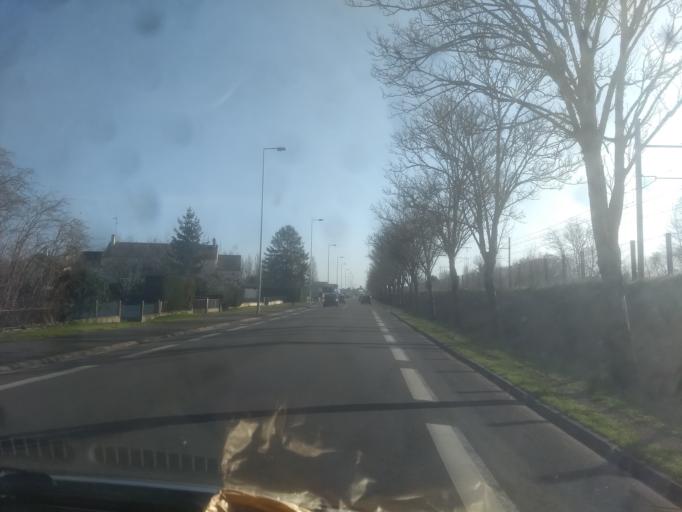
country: FR
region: Centre
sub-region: Departement du Cher
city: Bourges
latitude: 47.0945
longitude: 2.4148
